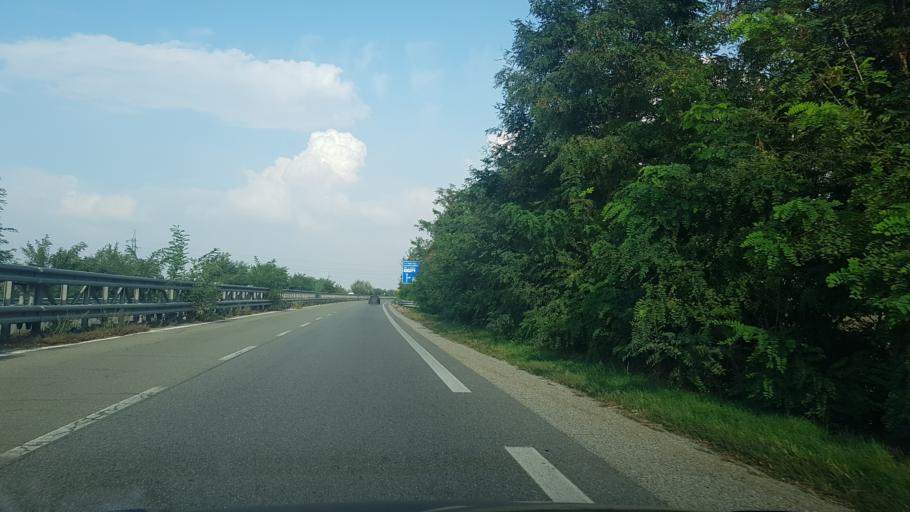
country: IT
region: Piedmont
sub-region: Provincia di Alessandria
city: Castellazzo Bormida
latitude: 44.8774
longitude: 8.5889
